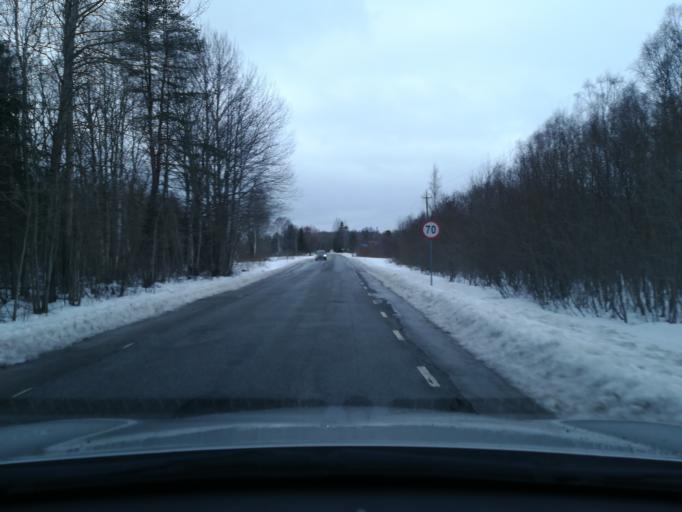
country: EE
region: Harju
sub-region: Nissi vald
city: Turba
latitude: 59.0701
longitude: 24.2499
